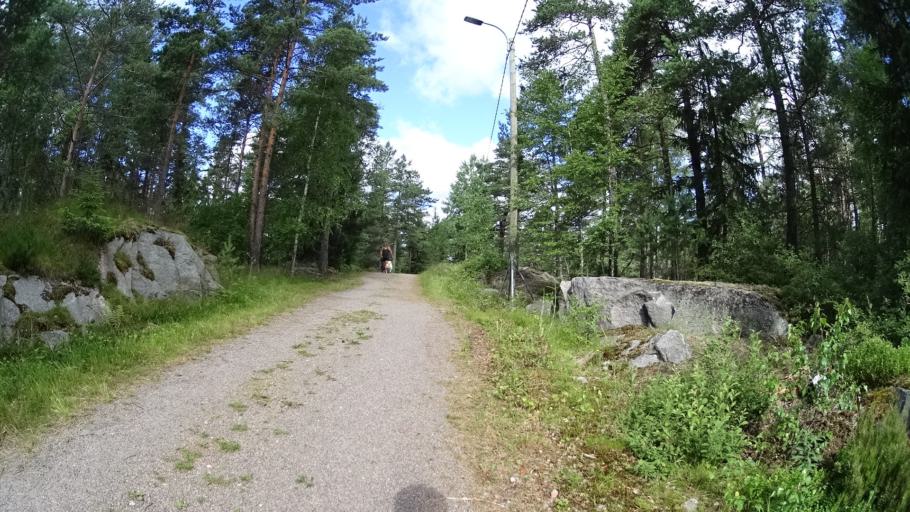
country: FI
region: Uusimaa
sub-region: Helsinki
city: Espoo
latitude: 60.2323
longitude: 24.6745
